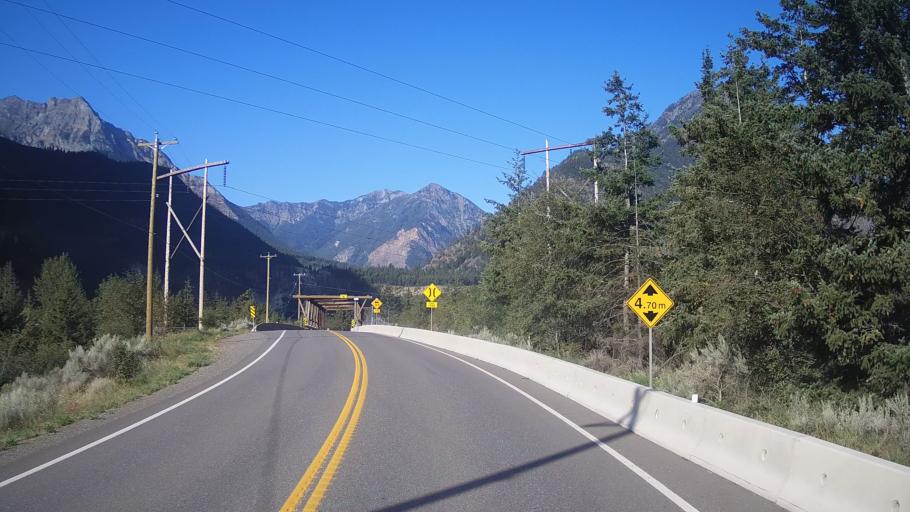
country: CA
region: British Columbia
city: Lillooet
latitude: 50.6699
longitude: -121.9716
